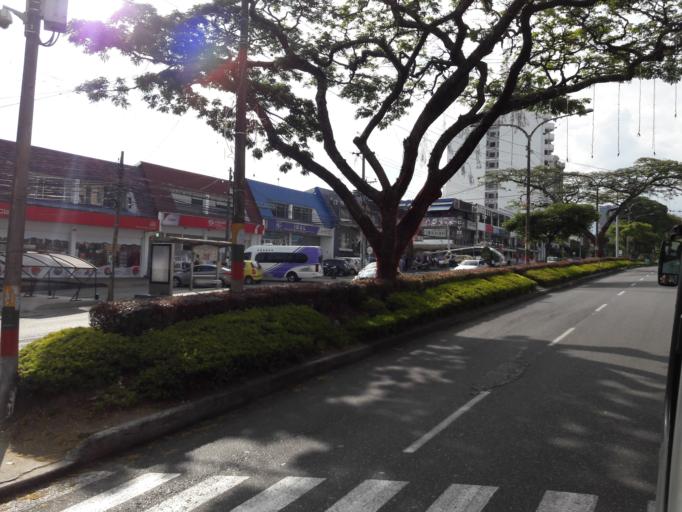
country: CO
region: Tolima
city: Ibague
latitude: 4.4369
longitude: -75.2146
